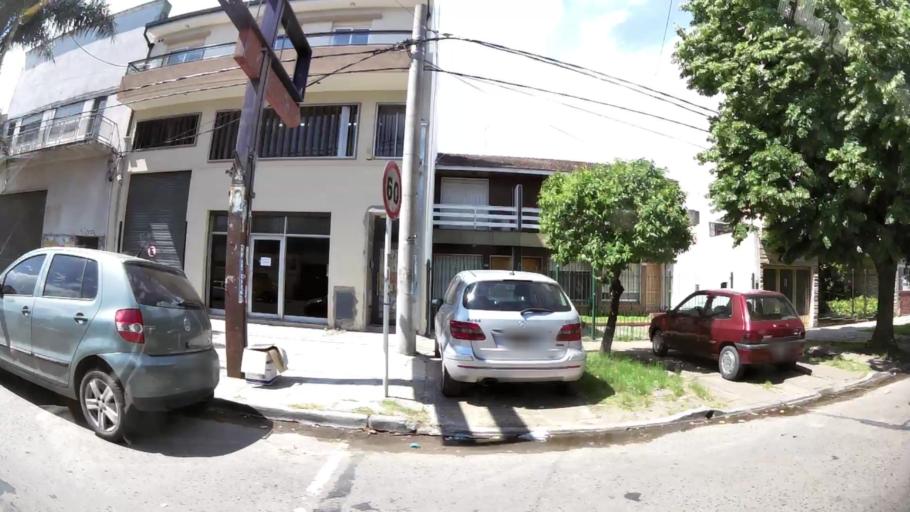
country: AR
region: Buenos Aires
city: San Justo
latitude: -34.6770
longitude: -58.5558
